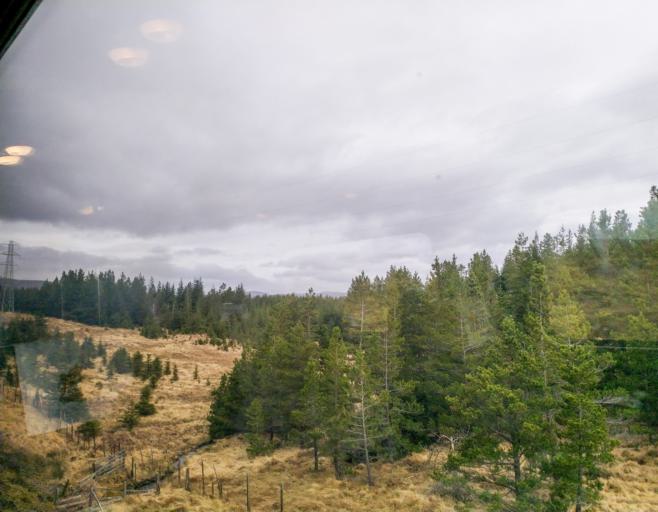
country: GB
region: Scotland
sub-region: Highland
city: Spean Bridge
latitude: 56.6597
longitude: -4.5644
